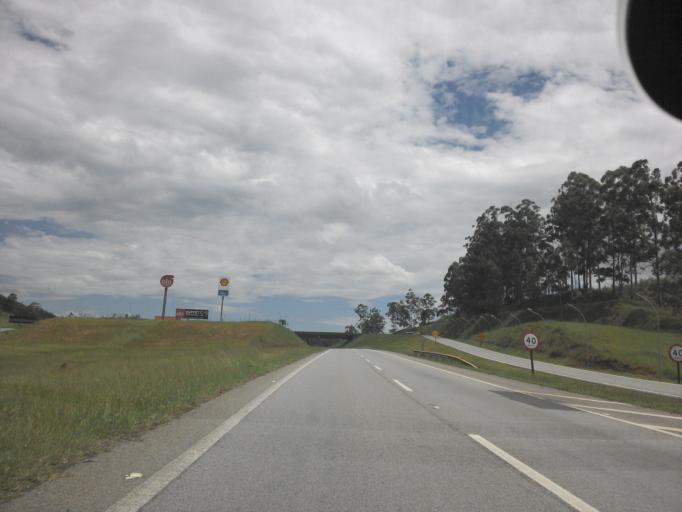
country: BR
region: Sao Paulo
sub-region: Cacapava
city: Cacapava
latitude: -23.0994
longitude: -45.6271
